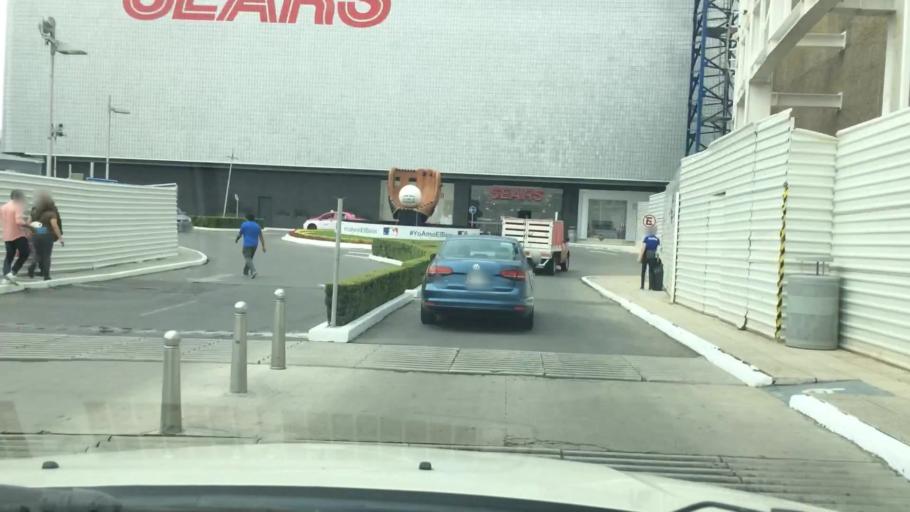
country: MX
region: Mexico City
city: Tlalpan
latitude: 19.3035
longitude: -99.1891
